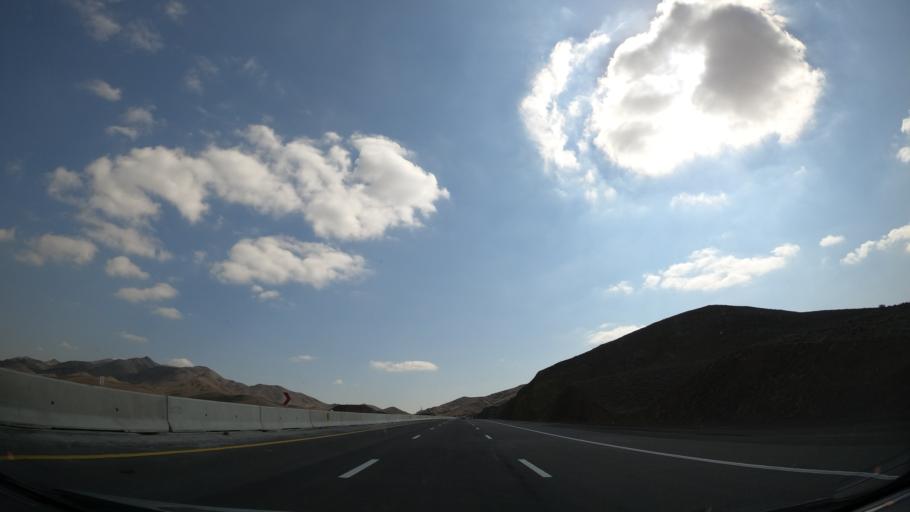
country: IR
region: Alborz
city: Nazarabad
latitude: 35.6924
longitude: 50.6335
